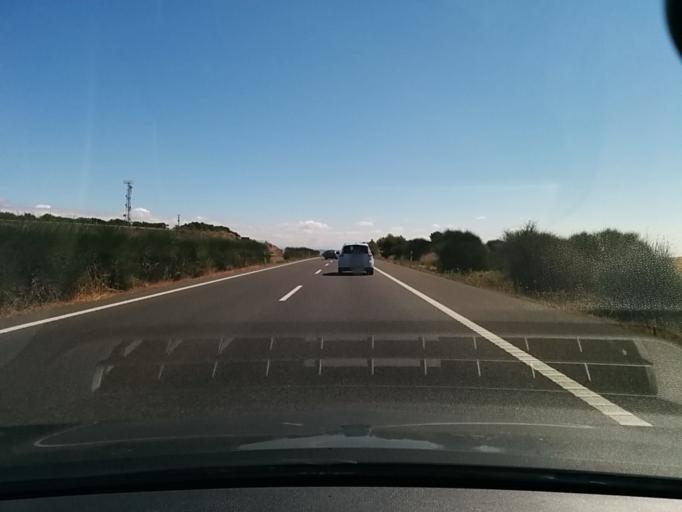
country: ES
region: Aragon
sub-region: Provincia de Huesca
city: Almudebar
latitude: 42.0689
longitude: -0.5129
